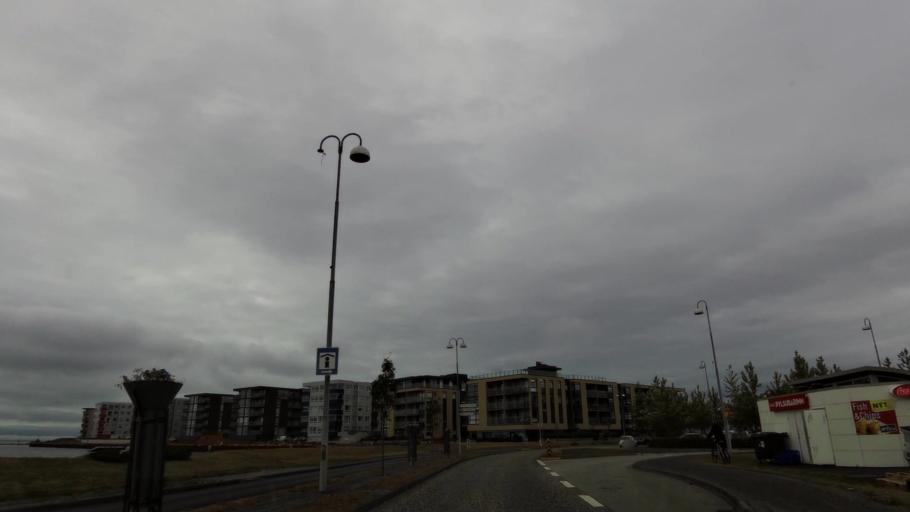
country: IS
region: Capital Region
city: Hafnarfjoerdur
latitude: 64.0684
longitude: -21.9587
